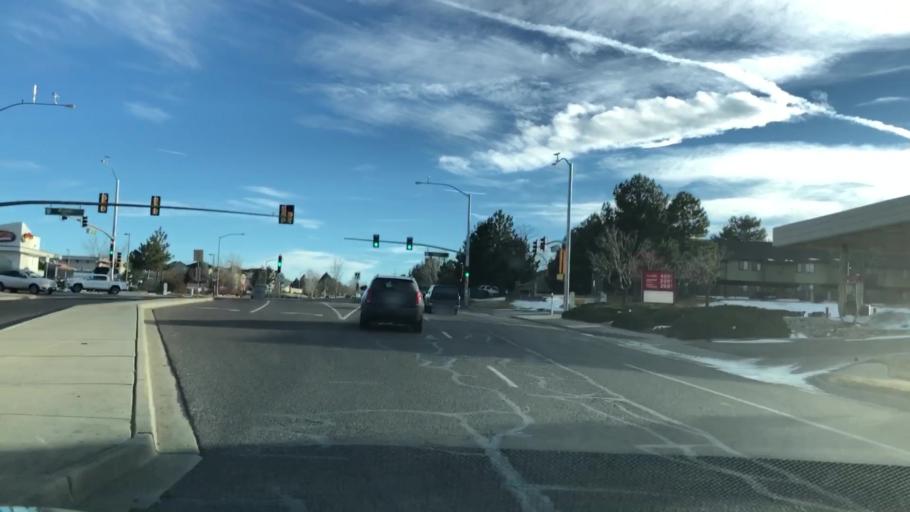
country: US
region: Colorado
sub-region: Adams County
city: Aurora
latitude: 39.6958
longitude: -104.7912
